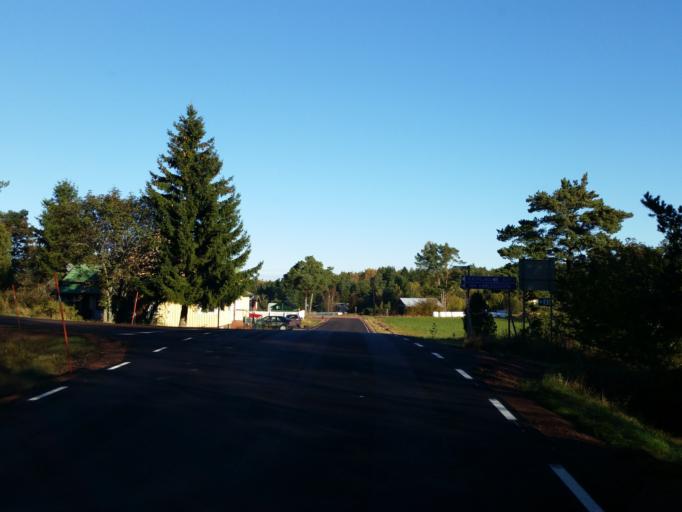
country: AX
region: Alands landsbygd
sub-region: Sund
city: Sund
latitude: 60.2291
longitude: 20.0906
